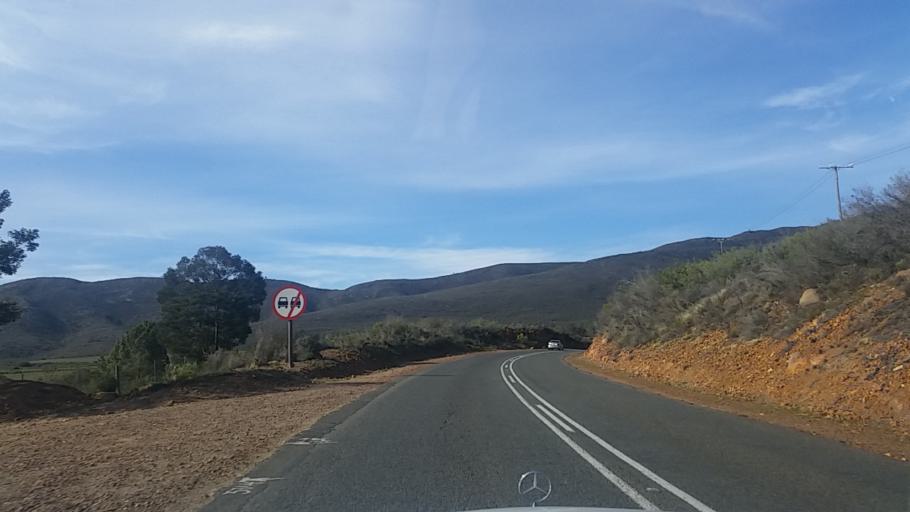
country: ZA
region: Western Cape
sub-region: Eden District Municipality
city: George
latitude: -33.8212
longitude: 22.3503
